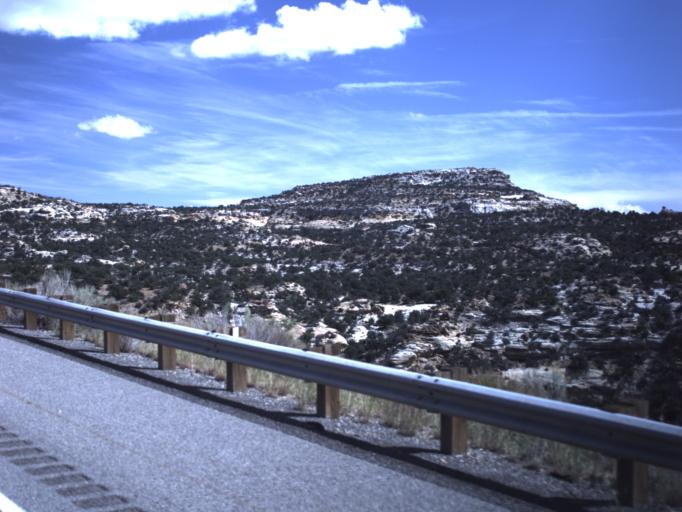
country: US
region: Utah
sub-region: Emery County
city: Ferron
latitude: 38.8593
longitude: -110.8219
